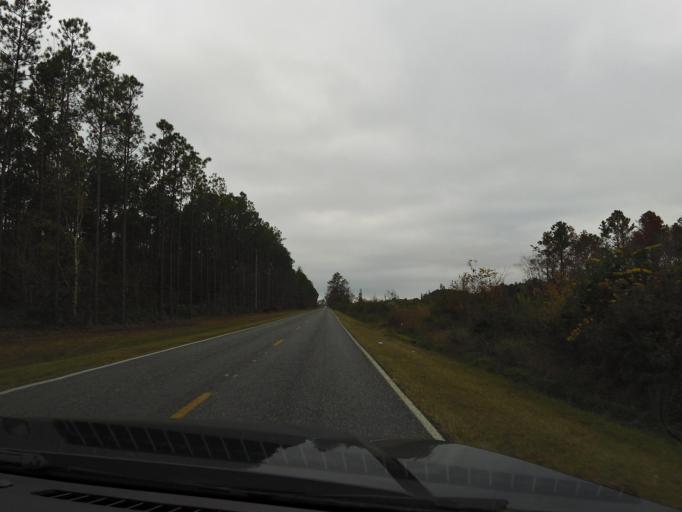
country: US
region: Georgia
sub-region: Charlton County
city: Folkston
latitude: 30.8900
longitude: -82.0621
